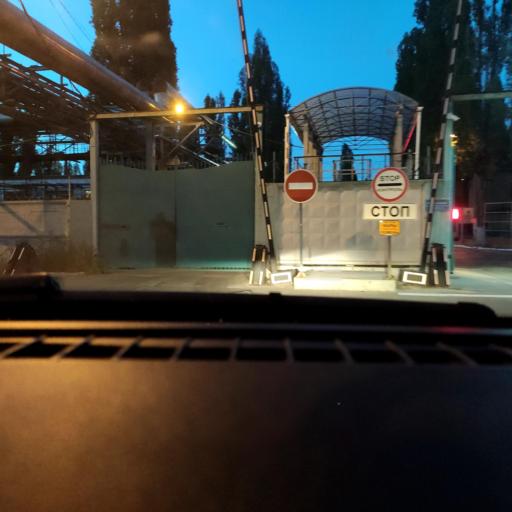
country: RU
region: Voronezj
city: Maslovka
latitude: 51.6248
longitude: 39.2463
